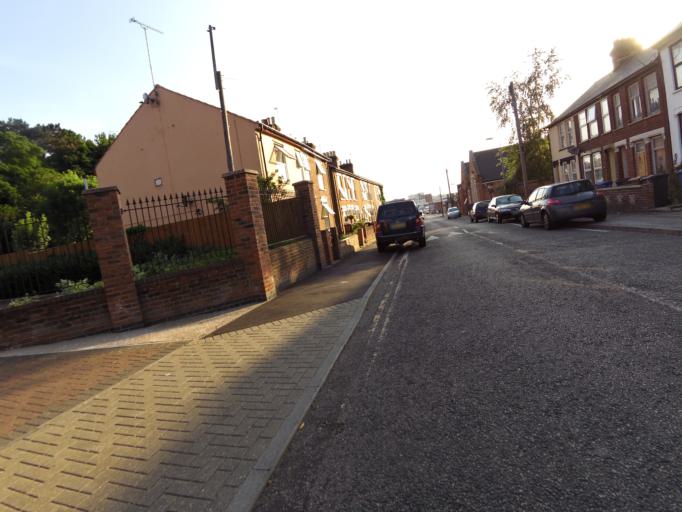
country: GB
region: England
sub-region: Suffolk
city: Ipswich
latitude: 52.0517
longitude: 1.1719
